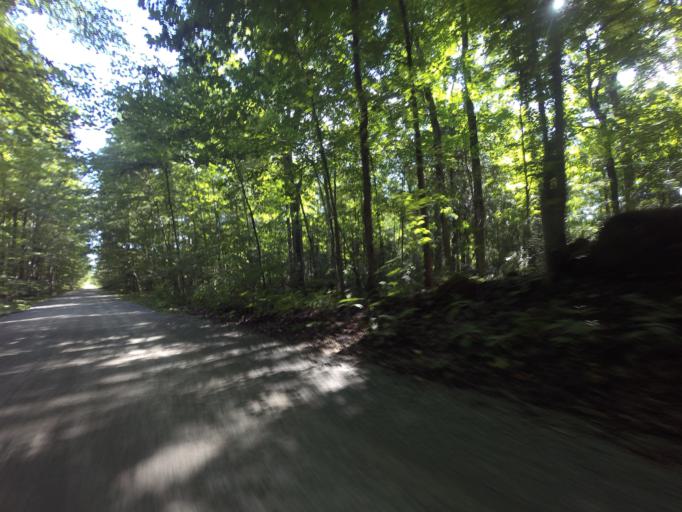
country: CA
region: Ontario
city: Omemee
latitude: 44.5920
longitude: -78.7286
